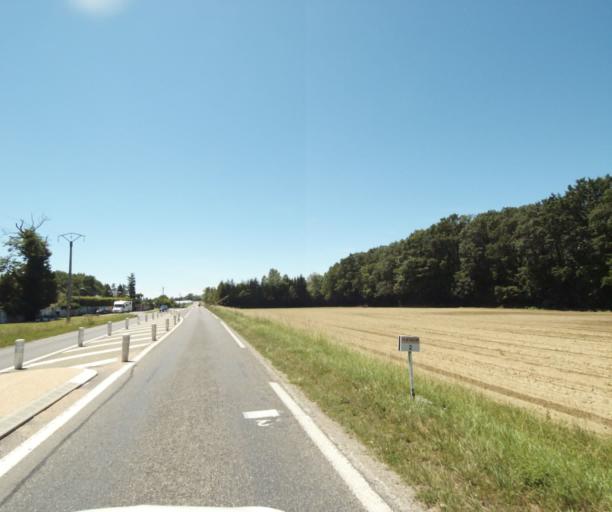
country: FR
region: Rhone-Alpes
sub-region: Departement de la Haute-Savoie
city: Veigy-Foncenex
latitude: 46.2848
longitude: 6.2619
